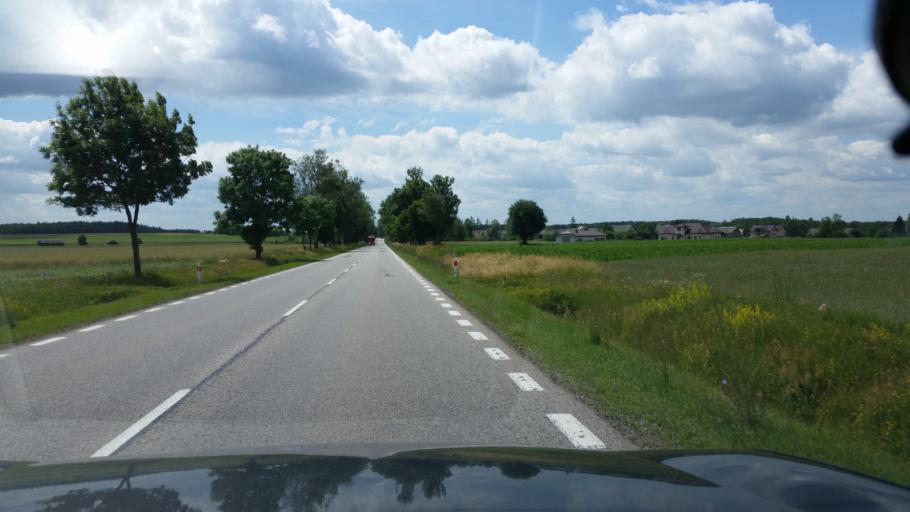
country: PL
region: Podlasie
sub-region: Powiat kolnenski
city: Stawiski
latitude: 53.3006
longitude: 22.1475
